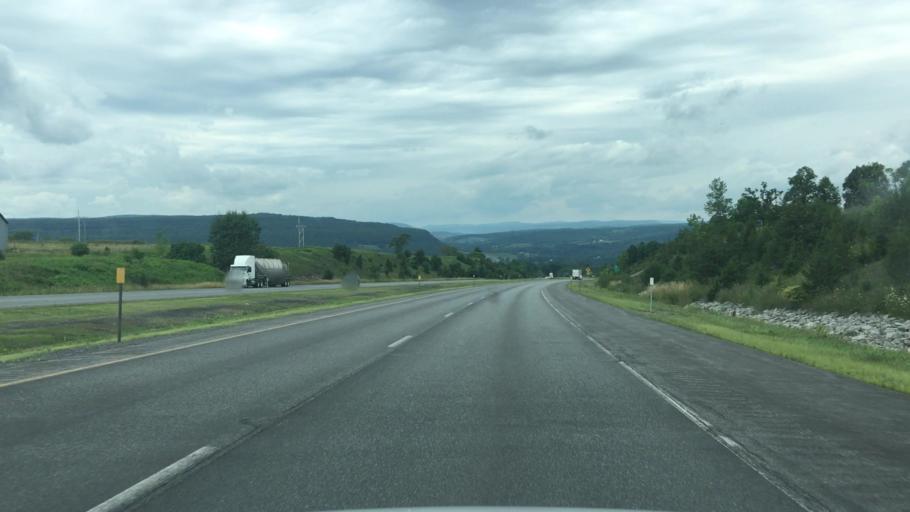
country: US
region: New York
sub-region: Schoharie County
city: Schoharie
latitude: 42.7125
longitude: -74.2824
